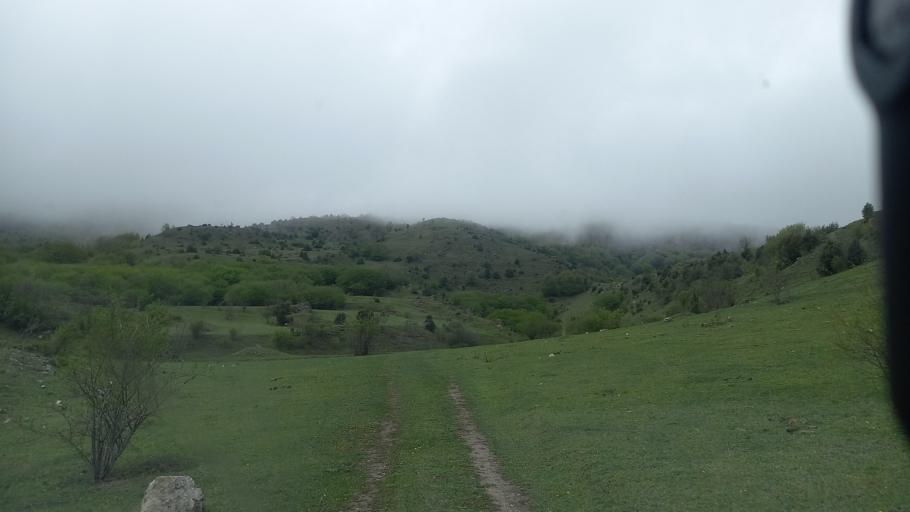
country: RU
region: Kabardino-Balkariya
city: Verkhnyaya Balkariya
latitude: 43.1687
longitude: 43.5001
